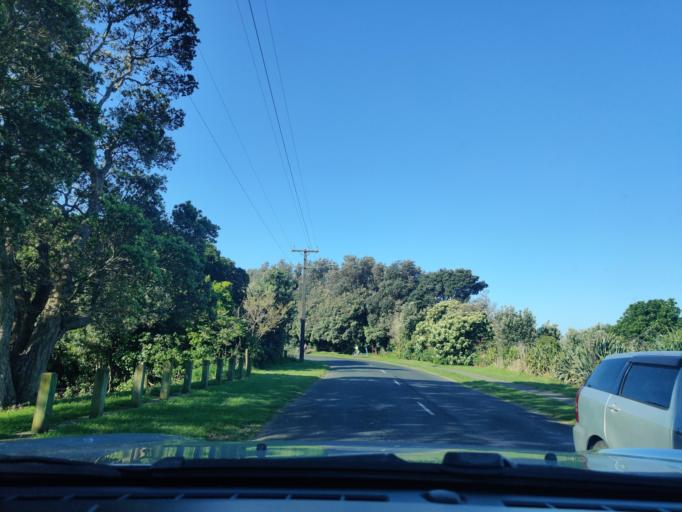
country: NZ
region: Taranaki
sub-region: New Plymouth District
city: New Plymouth
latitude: -39.0457
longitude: 174.1122
